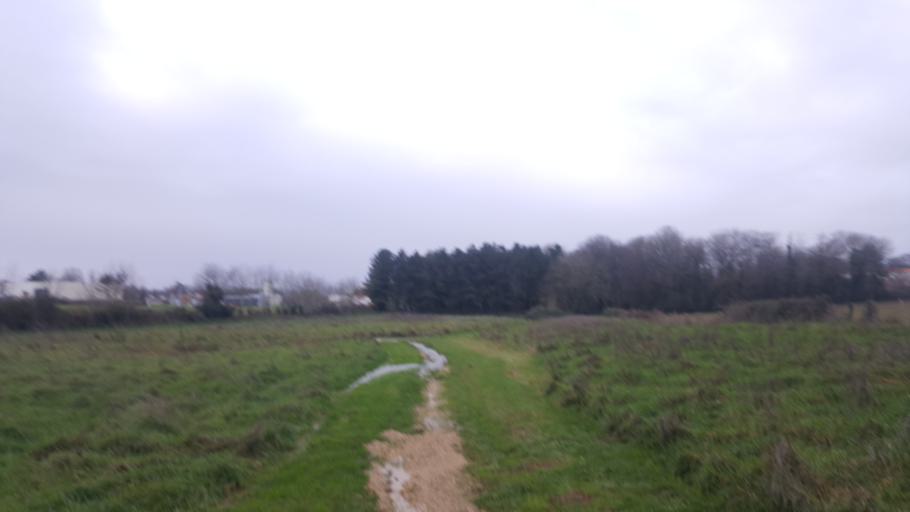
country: FR
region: Poitou-Charentes
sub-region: Departement des Deux-Sevres
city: Melle
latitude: 46.2280
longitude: -0.1317
